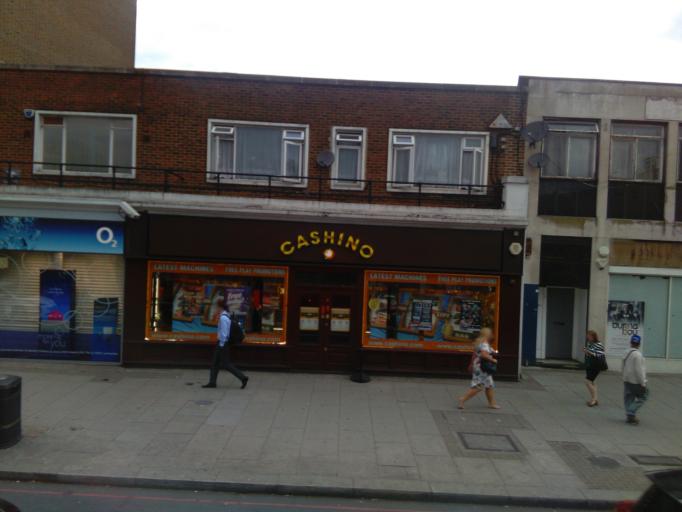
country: GB
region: England
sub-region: Greater London
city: Brixton Hill
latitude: 51.4441
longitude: -0.1523
